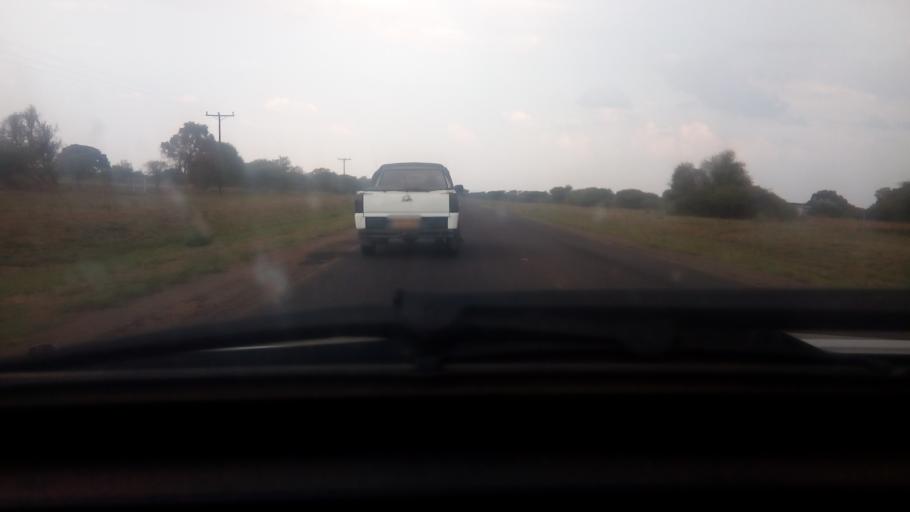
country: BW
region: Kweneng
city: Metsemotlhaba
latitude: -24.4828
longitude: 25.7335
